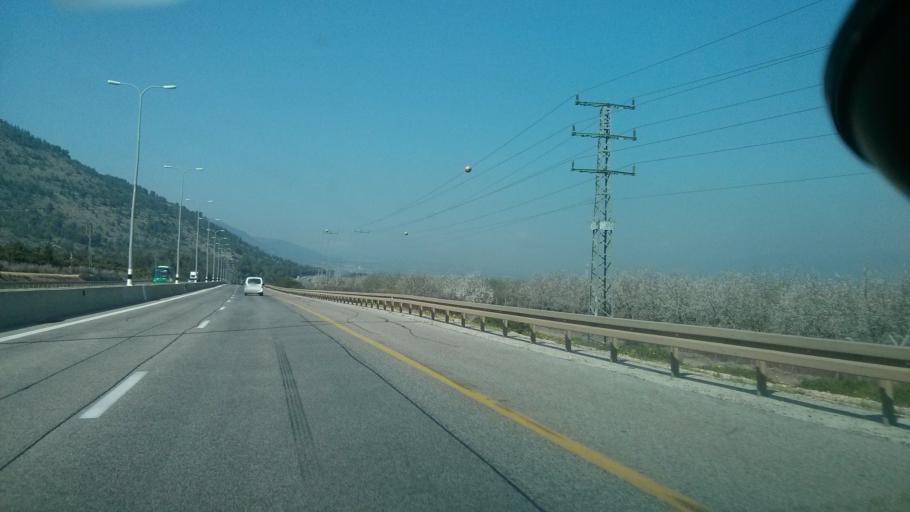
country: IL
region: Northern District
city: Rosh Pinna
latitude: 33.0746
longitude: 35.5763
